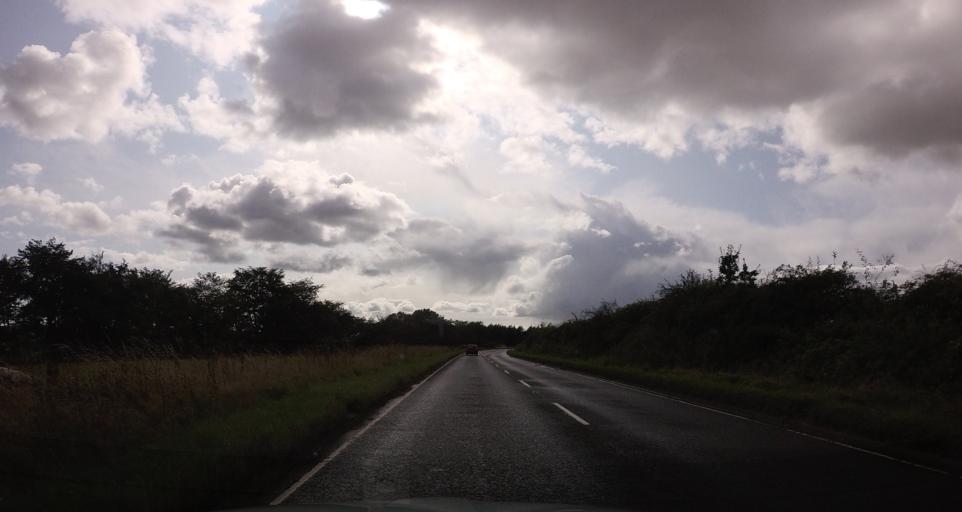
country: GB
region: Scotland
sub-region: Perth and Kinross
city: Kinross
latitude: 56.2056
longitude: -3.4671
